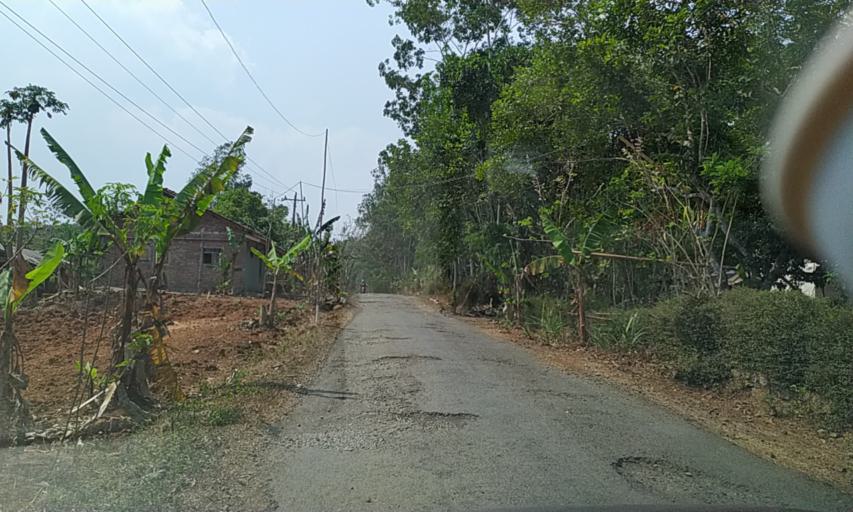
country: ID
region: Central Java
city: Karanggintung
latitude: -7.4494
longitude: 108.8554
